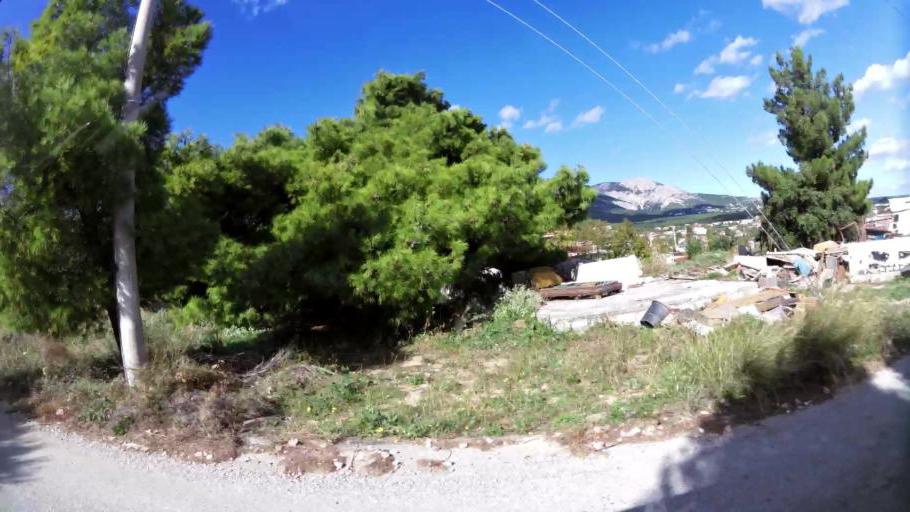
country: GR
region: Attica
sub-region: Nomarchia Anatolikis Attikis
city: Acharnes
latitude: 38.1157
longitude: 23.7248
